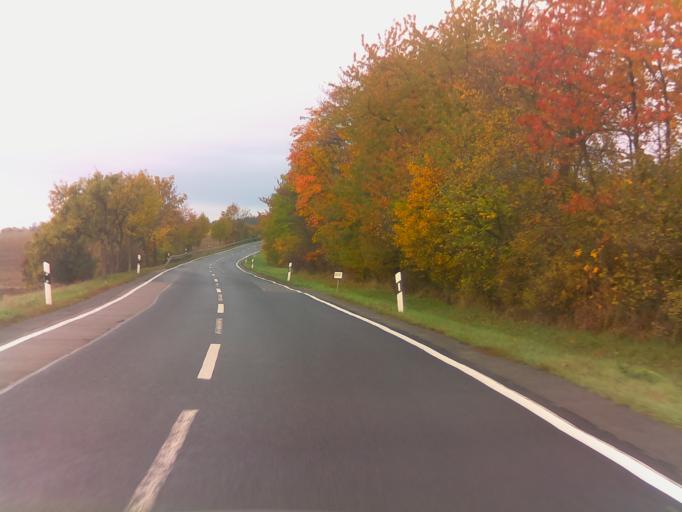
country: DE
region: Thuringia
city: Stadtilm
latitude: 50.7611
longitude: 11.1300
